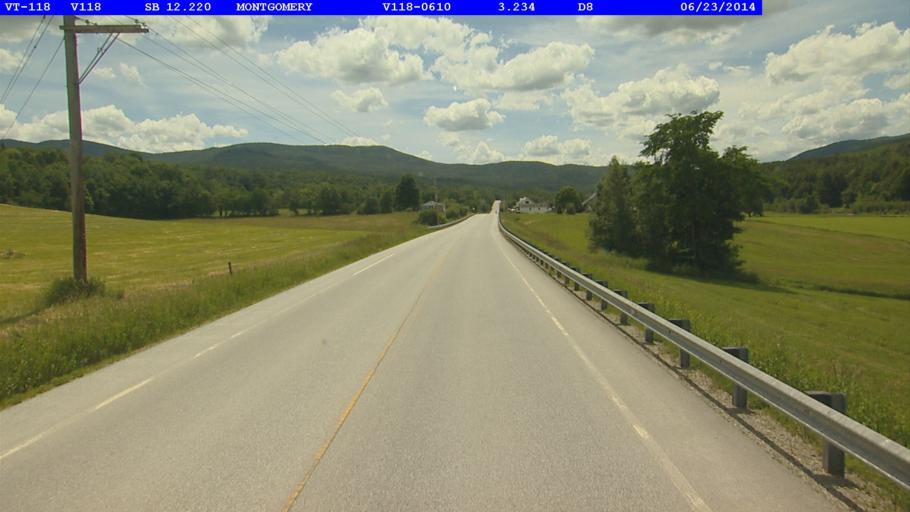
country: US
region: Vermont
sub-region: Franklin County
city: Richford
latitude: 44.8443
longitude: -72.6099
